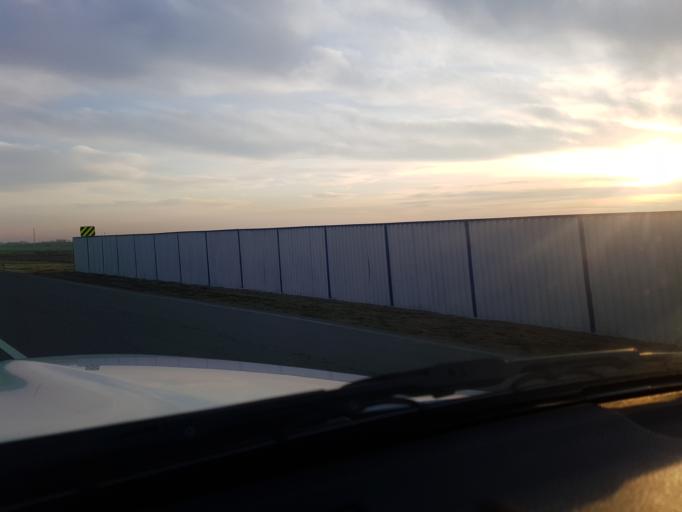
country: TM
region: Ahal
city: Abadan
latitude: 38.1710
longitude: 58.3835
